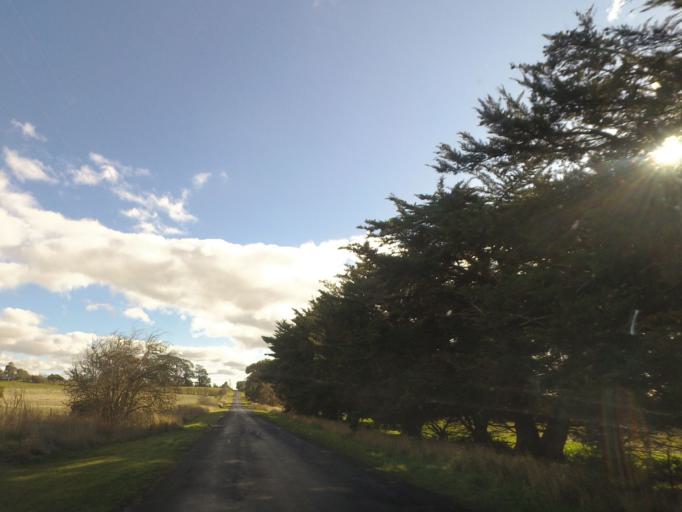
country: AU
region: Victoria
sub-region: Mount Alexander
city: Castlemaine
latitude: -37.2533
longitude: 144.4187
